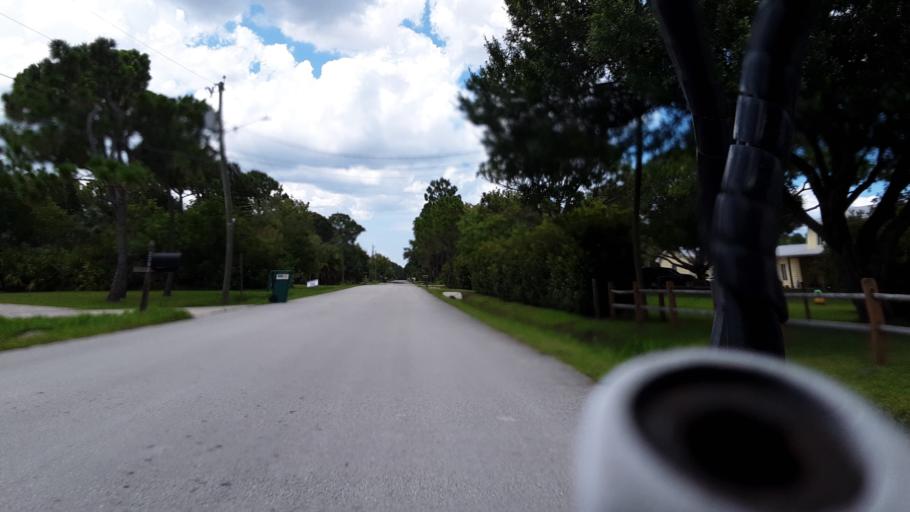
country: US
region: Florida
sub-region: Brevard County
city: Malabar
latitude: 27.9853
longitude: -80.5753
